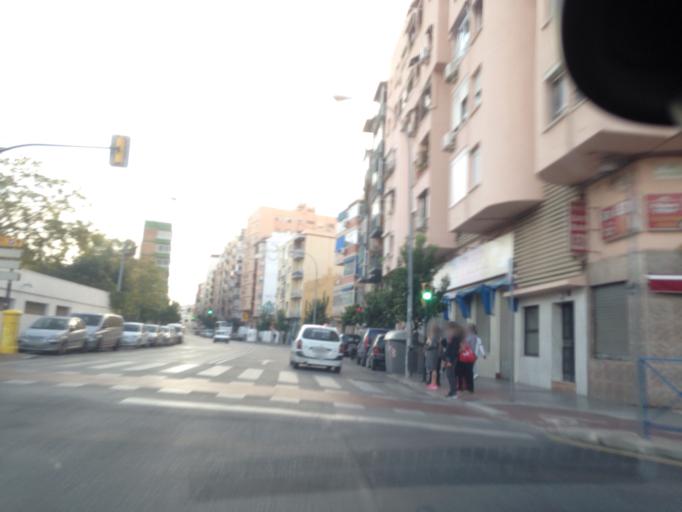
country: ES
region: Andalusia
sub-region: Provincia de Malaga
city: Malaga
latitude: 36.7298
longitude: -4.4341
